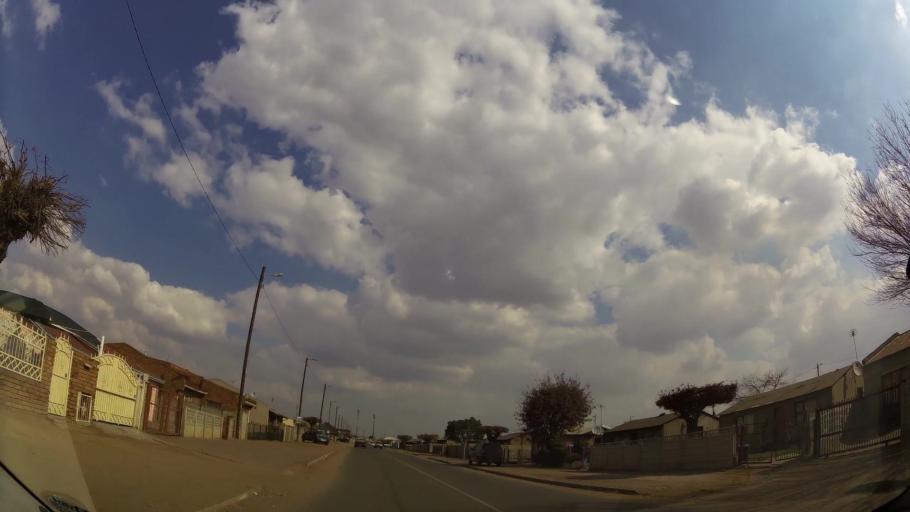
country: ZA
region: Gauteng
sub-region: Ekurhuleni Metropolitan Municipality
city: Brakpan
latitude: -26.1378
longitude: 28.4265
